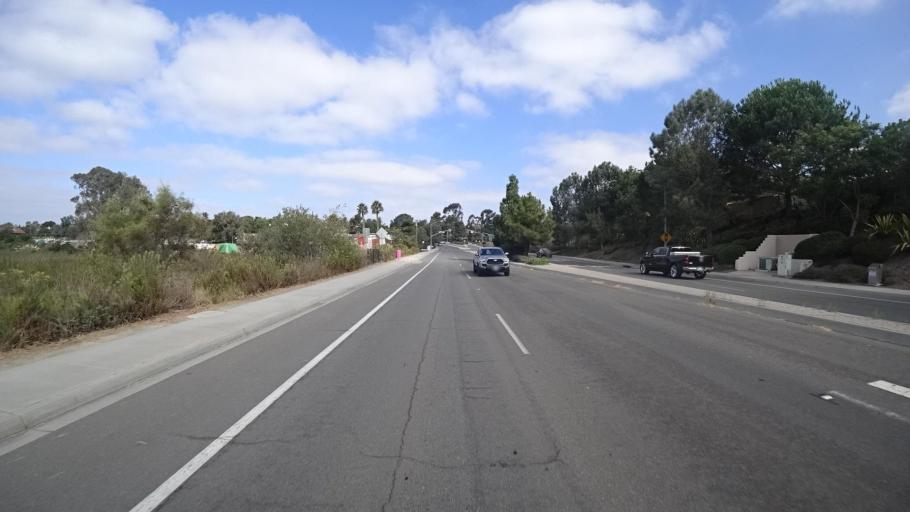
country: US
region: California
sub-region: San Diego County
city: Encinitas
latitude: 33.0666
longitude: -117.2453
